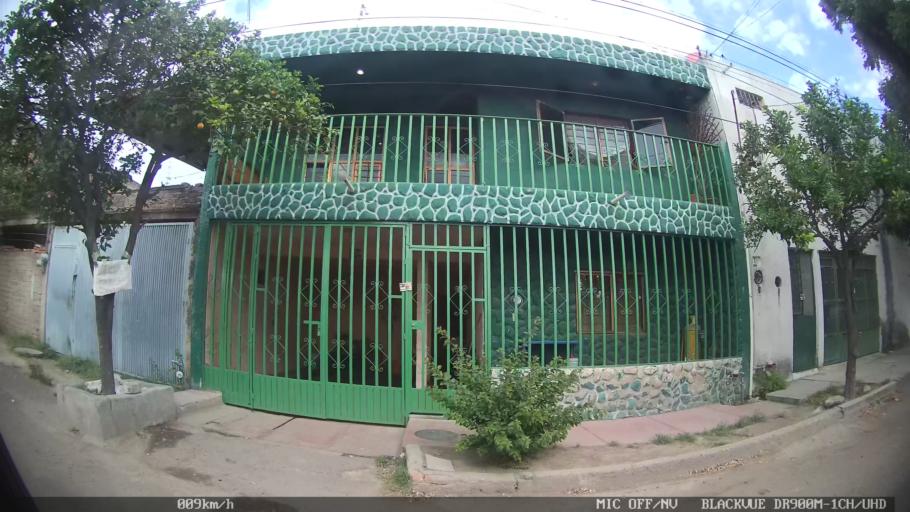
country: MX
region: Jalisco
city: Tonala
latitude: 20.6640
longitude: -103.2337
